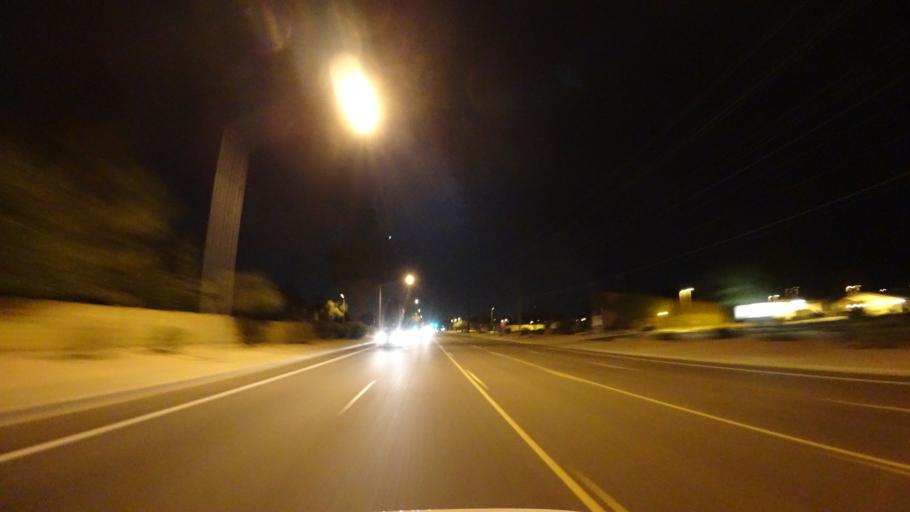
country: US
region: Arizona
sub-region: Maricopa County
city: Gilbert
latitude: 33.4374
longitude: -111.6897
